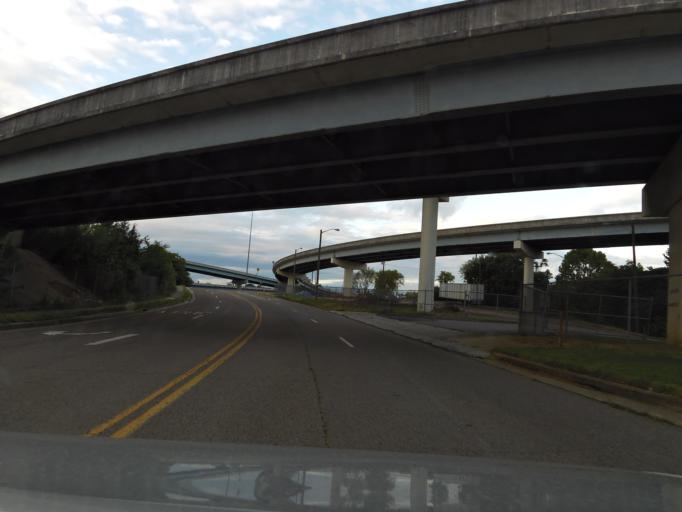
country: US
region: Tennessee
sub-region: Knox County
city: Knoxville
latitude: 35.9668
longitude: -83.9278
